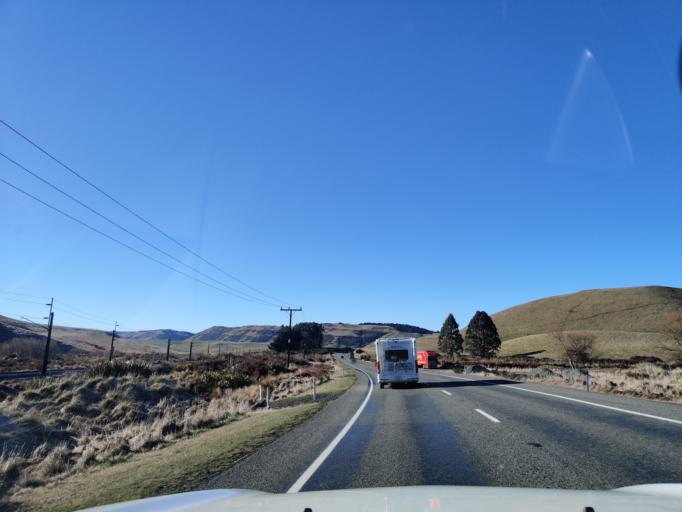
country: NZ
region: Manawatu-Wanganui
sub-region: Ruapehu District
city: Waiouru
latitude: -39.5064
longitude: 175.6755
